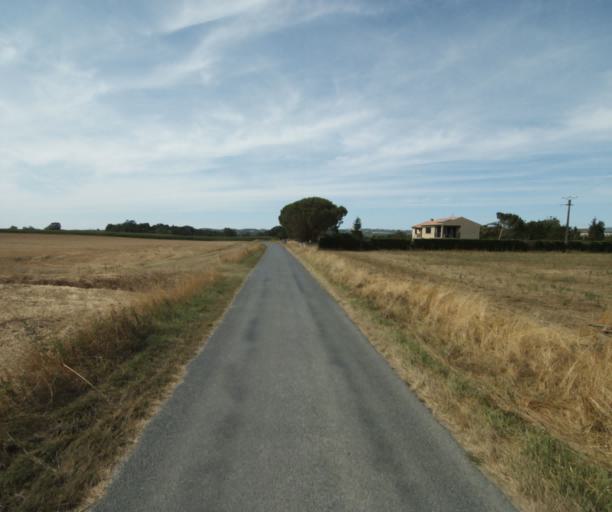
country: FR
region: Midi-Pyrenees
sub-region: Departement du Tarn
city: Soreze
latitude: 43.5092
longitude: 2.0449
